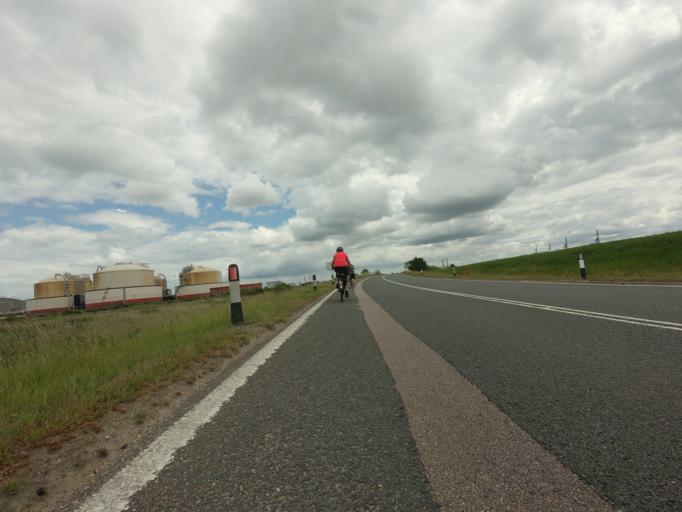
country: GB
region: England
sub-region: Medway
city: Allhallows
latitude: 51.4486
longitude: 0.6713
